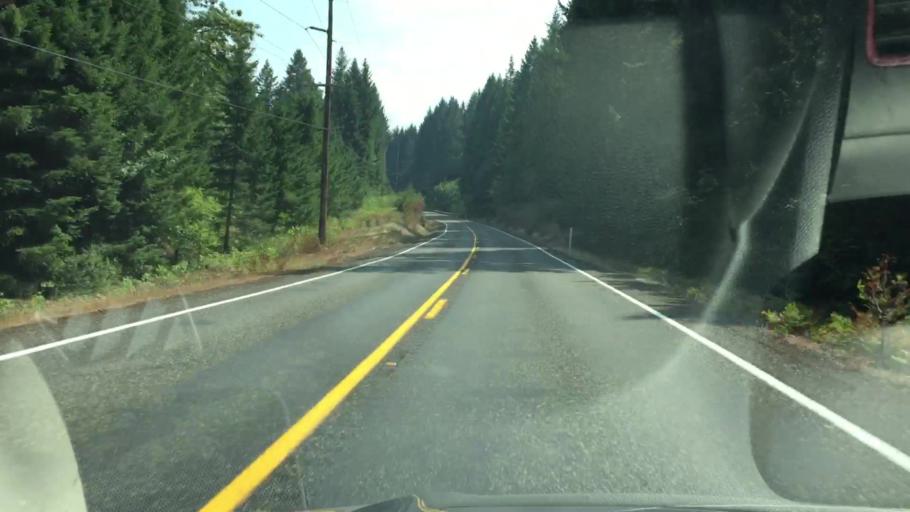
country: US
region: Washington
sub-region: Klickitat County
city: White Salmon
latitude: 45.8794
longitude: -121.5207
